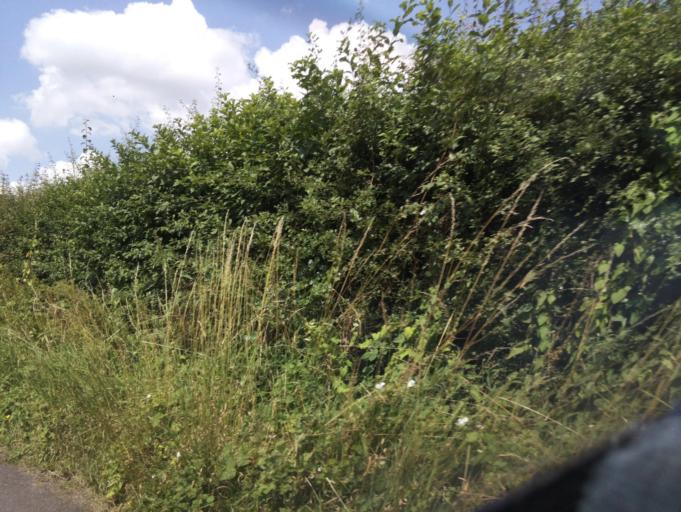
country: GB
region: England
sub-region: Wiltshire
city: Leigh
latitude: 51.5884
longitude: -1.9113
